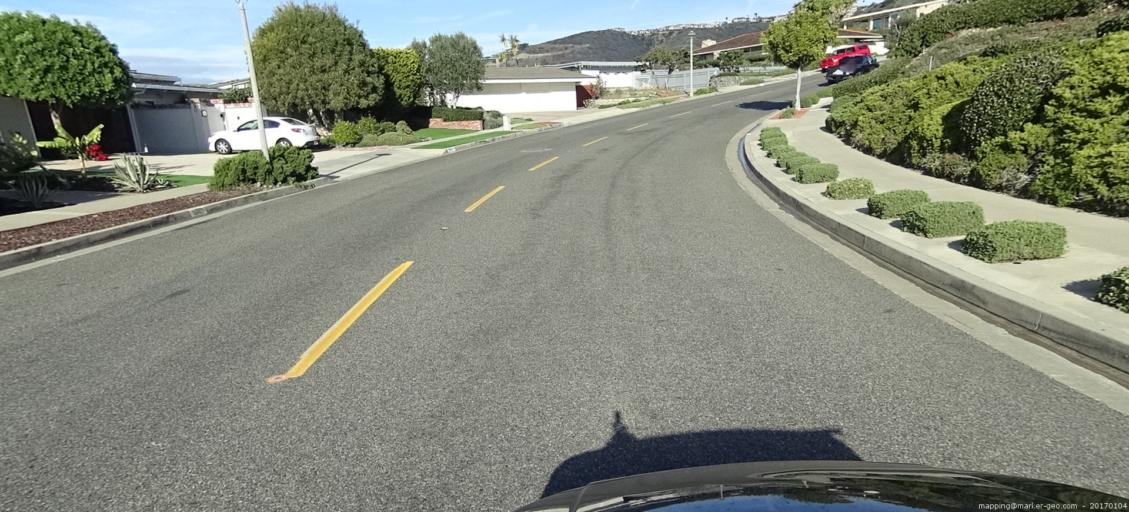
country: US
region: California
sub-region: Orange County
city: Dana Point
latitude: 33.4892
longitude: -117.7250
